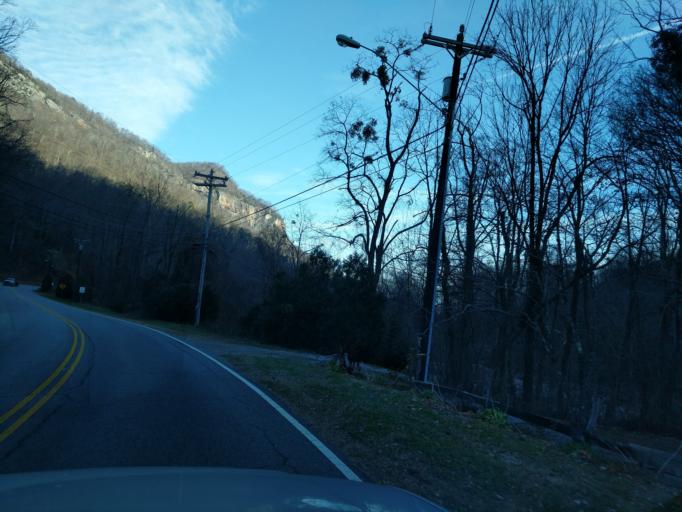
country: US
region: North Carolina
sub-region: Rutherford County
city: Lake Lure
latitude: 35.4424
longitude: -82.2638
